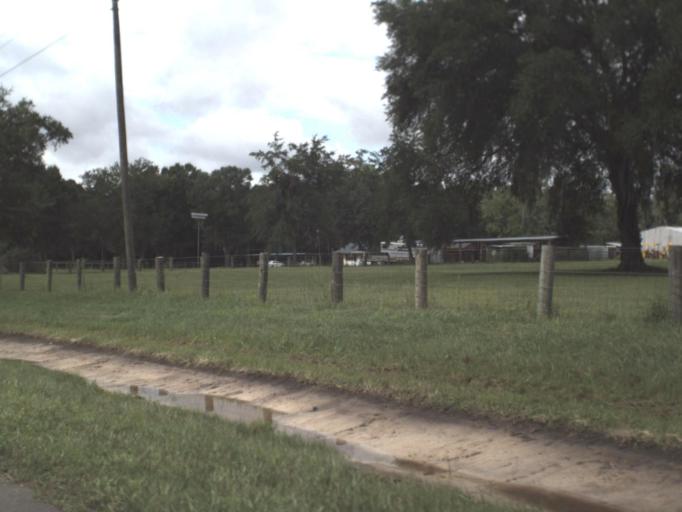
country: US
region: Florida
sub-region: Columbia County
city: Five Points
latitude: 30.2999
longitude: -82.6308
